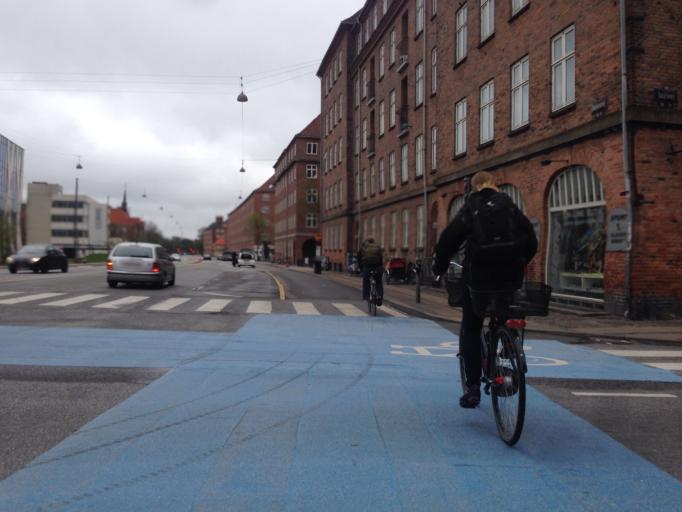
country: DK
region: Capital Region
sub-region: Kobenhavn
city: Copenhagen
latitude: 55.6991
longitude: 12.5542
